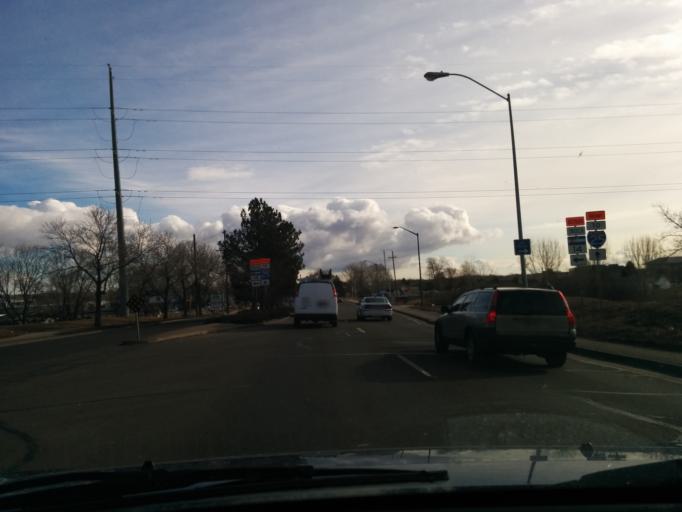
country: US
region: Colorado
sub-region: Larimer County
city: Fort Collins
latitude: 40.5671
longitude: -105.0421
